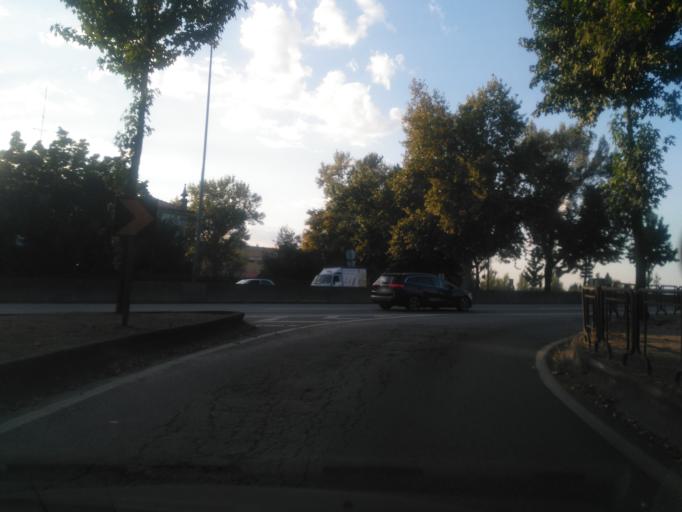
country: PT
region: Braga
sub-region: Braga
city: Braga
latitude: 41.5528
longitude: -8.4308
